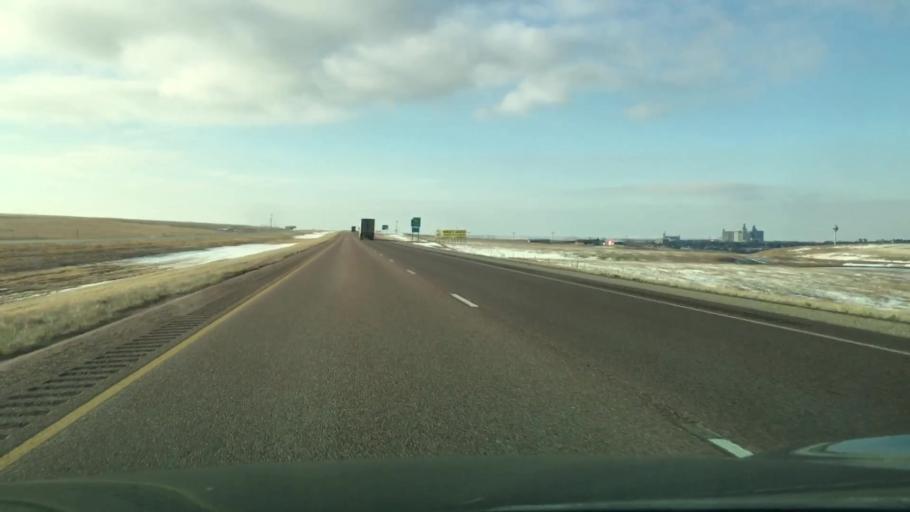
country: US
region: South Dakota
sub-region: Lyman County
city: Kennebec
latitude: 43.8885
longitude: -99.8403
